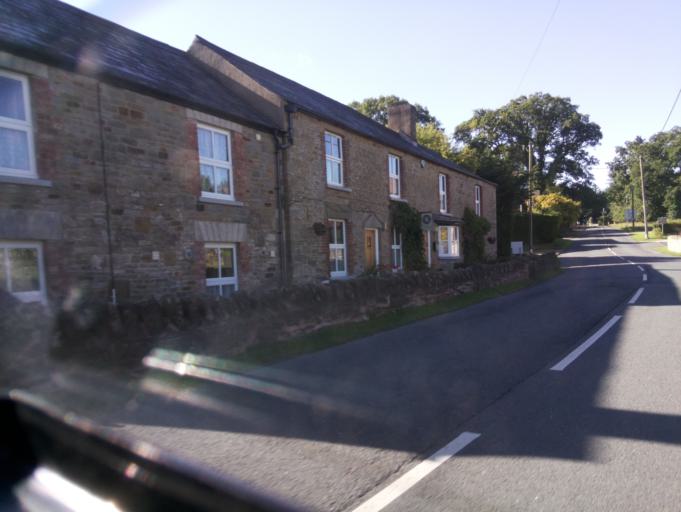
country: GB
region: England
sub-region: Gloucestershire
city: Coleford
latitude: 51.8153
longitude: -2.6231
